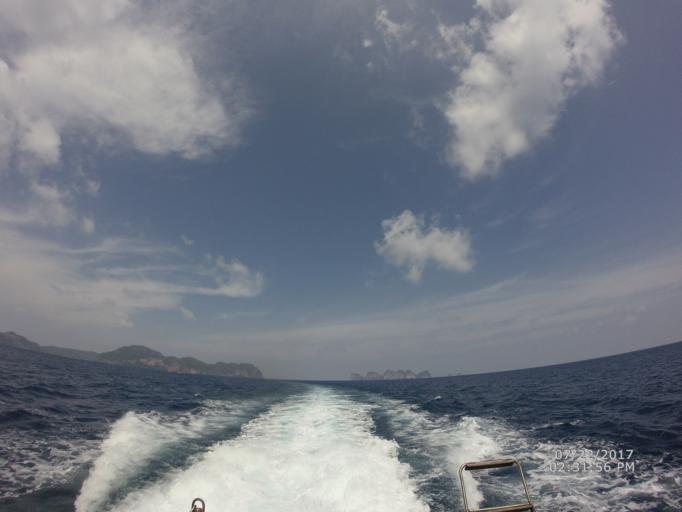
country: TH
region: Phangnga
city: Ban Phru Nai
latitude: 7.7397
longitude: 98.7140
